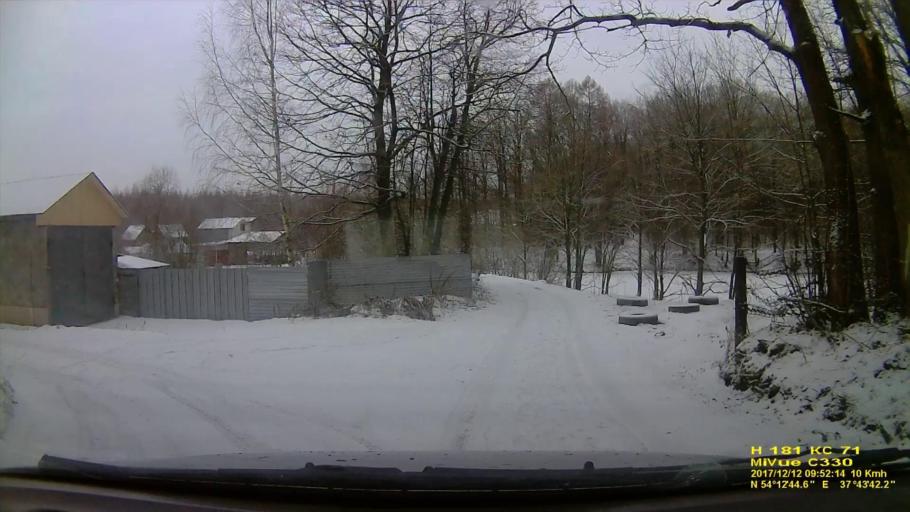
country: RU
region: Tula
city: Tula
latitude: 54.2123
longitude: 37.7284
